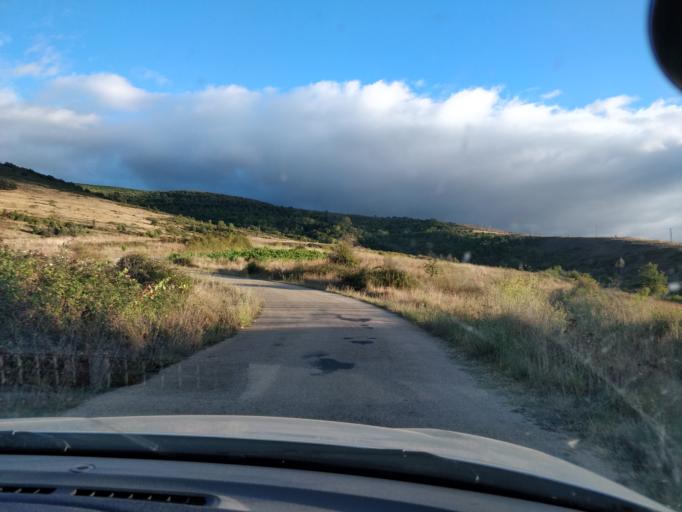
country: ES
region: Castille and Leon
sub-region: Provincia de Leon
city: Borrenes
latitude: 42.4901
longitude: -6.7019
